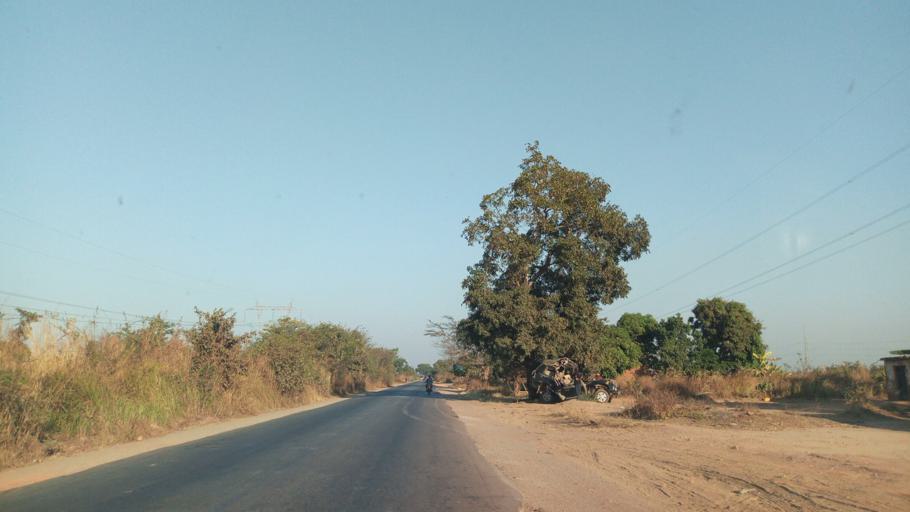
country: CD
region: Katanga
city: Likasi
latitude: -11.1237
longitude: 27.0348
